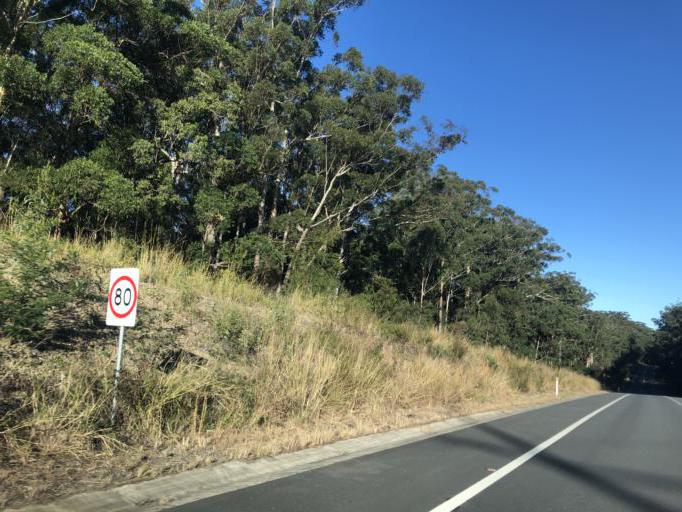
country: AU
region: New South Wales
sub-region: Nambucca Shire
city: Nambucca
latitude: -30.5454
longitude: 153.0069
